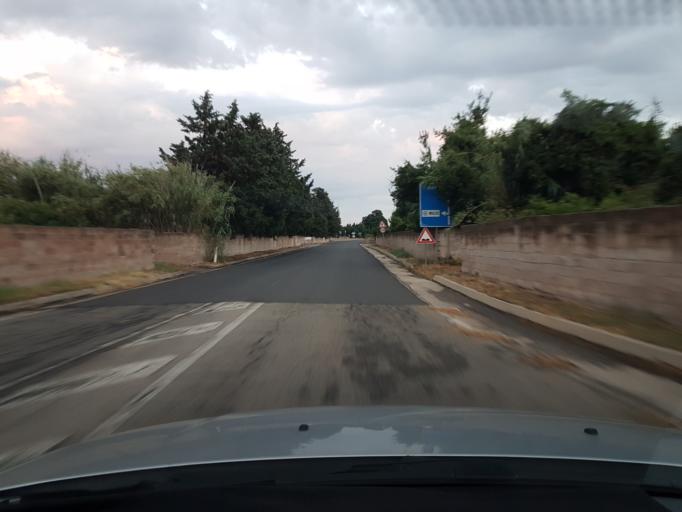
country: IT
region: Sardinia
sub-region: Provincia di Oristano
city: Milis
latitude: 40.0455
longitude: 8.6324
